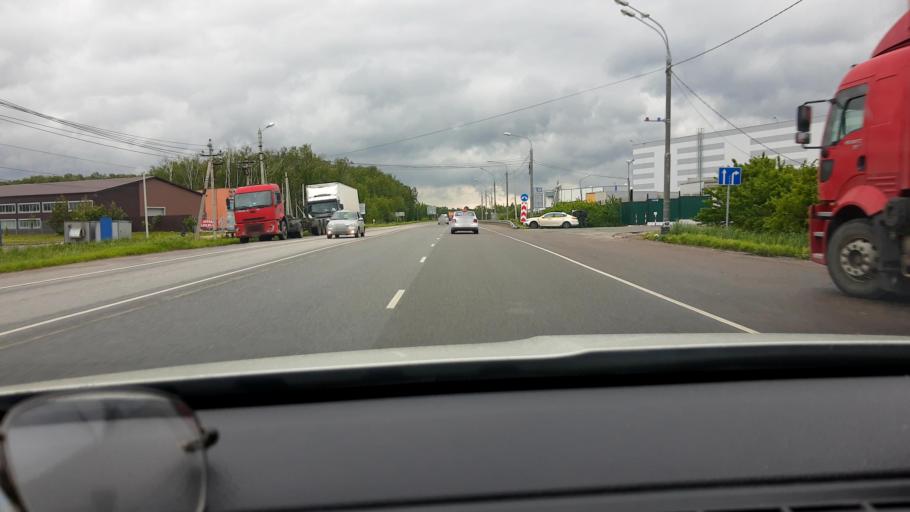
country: RU
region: Moskovskaya
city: Gorki-Leninskiye
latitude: 55.5118
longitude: 37.7864
